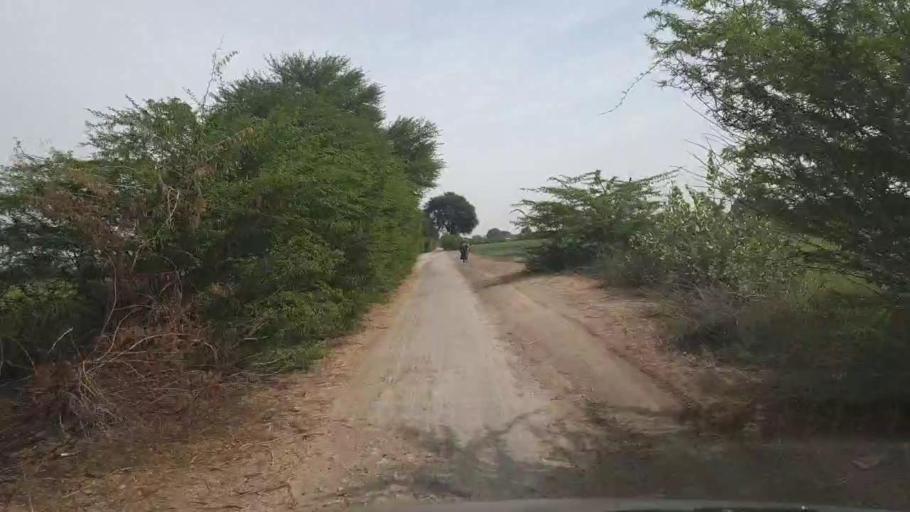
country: PK
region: Sindh
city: Umarkot
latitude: 25.2515
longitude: 69.7040
